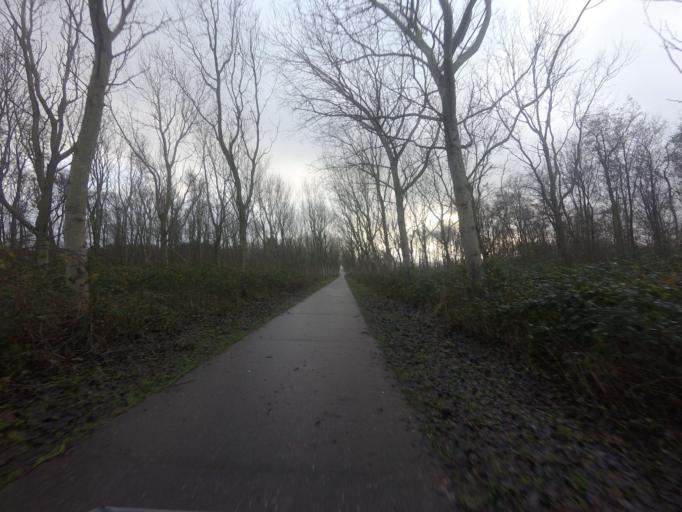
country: NL
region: North Holland
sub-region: Gemeente Texel
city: Den Burg
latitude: 53.1618
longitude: 4.8521
